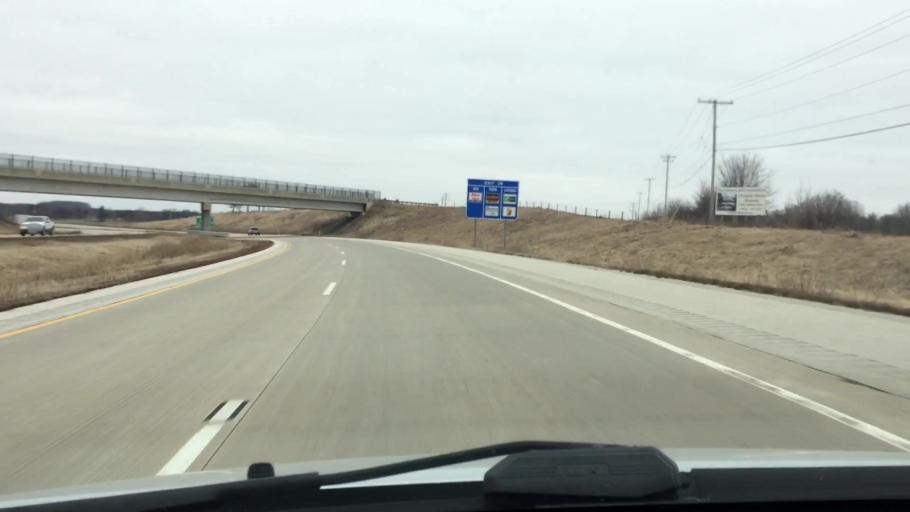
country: US
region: Wisconsin
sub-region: Jefferson County
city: Watertown
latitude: 43.1498
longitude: -88.7347
